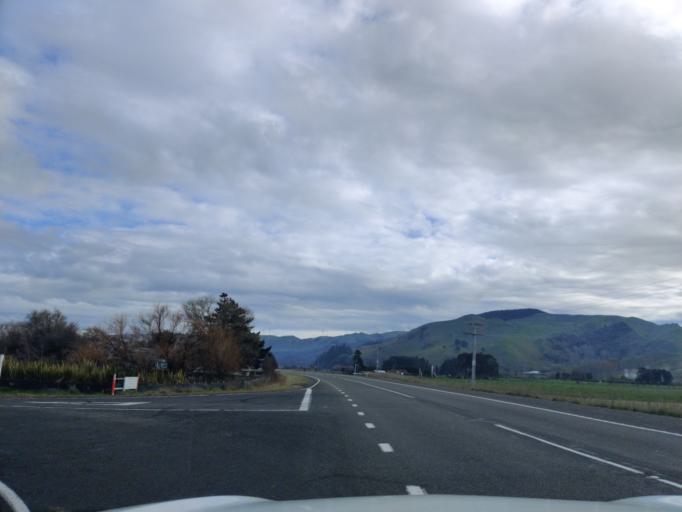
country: NZ
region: Manawatu-Wanganui
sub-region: Palmerston North City
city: Palmerston North
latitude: -40.3333
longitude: 175.8466
